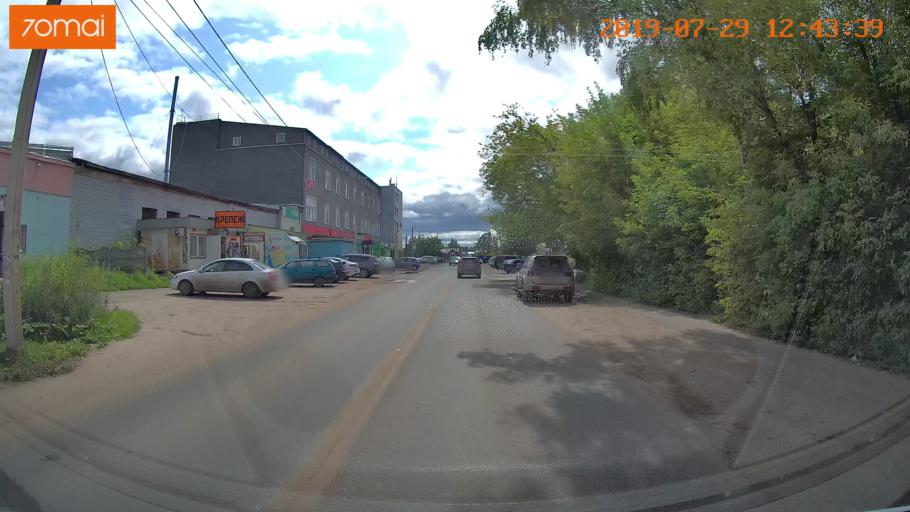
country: RU
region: Ivanovo
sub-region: Gorod Ivanovo
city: Ivanovo
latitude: 57.0010
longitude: 40.9305
